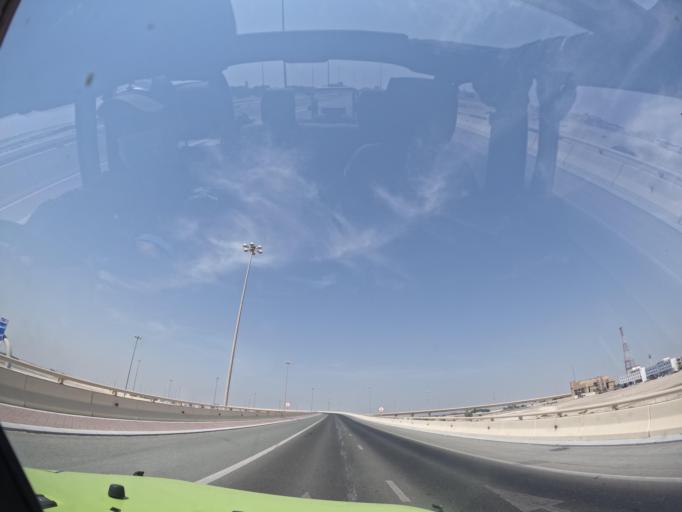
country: AE
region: Abu Dhabi
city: Abu Dhabi
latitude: 24.3072
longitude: 54.6065
